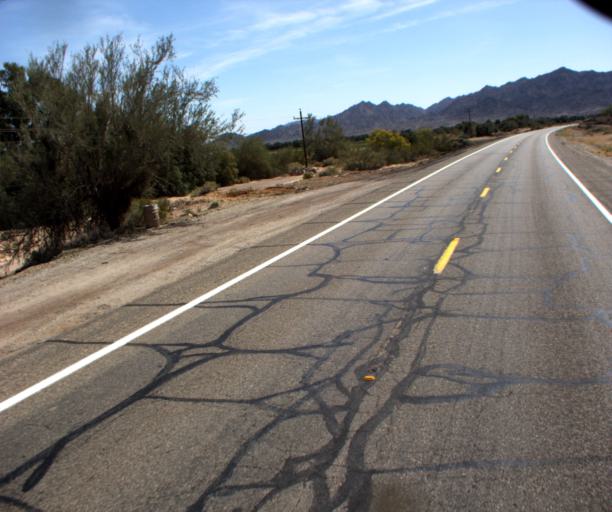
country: US
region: Arizona
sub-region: Yuma County
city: Fortuna Foothills
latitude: 32.7871
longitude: -114.3813
